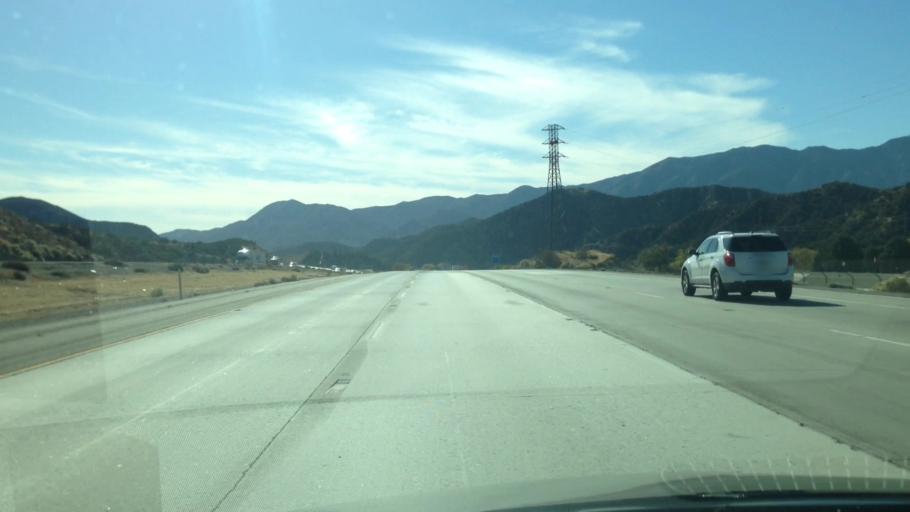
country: US
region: California
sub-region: Kern County
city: Lebec
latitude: 34.7189
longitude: -118.7990
